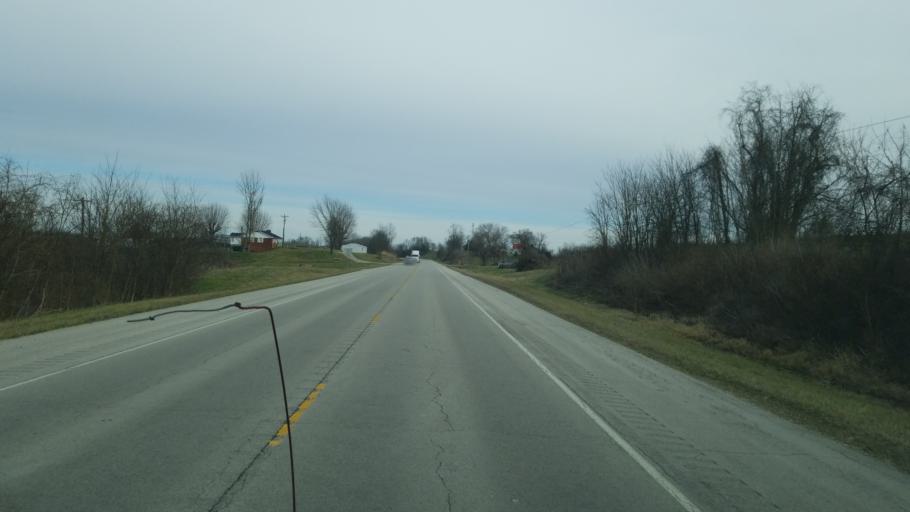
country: US
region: Kentucky
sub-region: Robertson County
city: Mount Olivet
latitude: 38.4615
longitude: -83.9244
